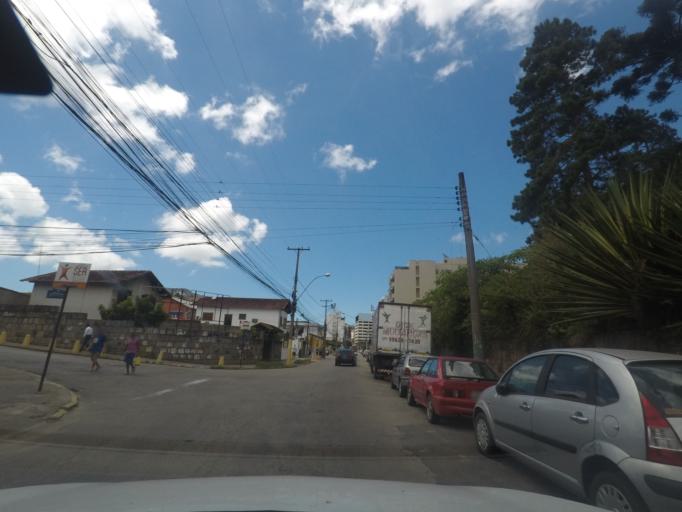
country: BR
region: Rio de Janeiro
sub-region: Teresopolis
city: Teresopolis
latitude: -22.4069
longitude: -42.9673
